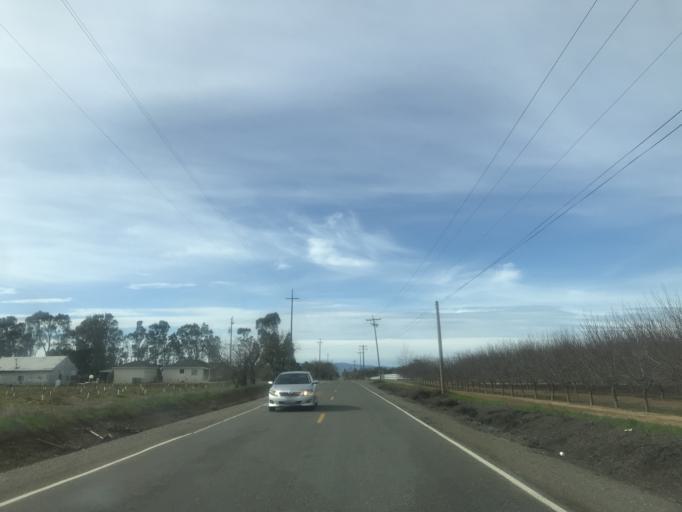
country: US
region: California
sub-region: Yolo County
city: Woodland
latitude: 38.6634
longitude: -121.8521
